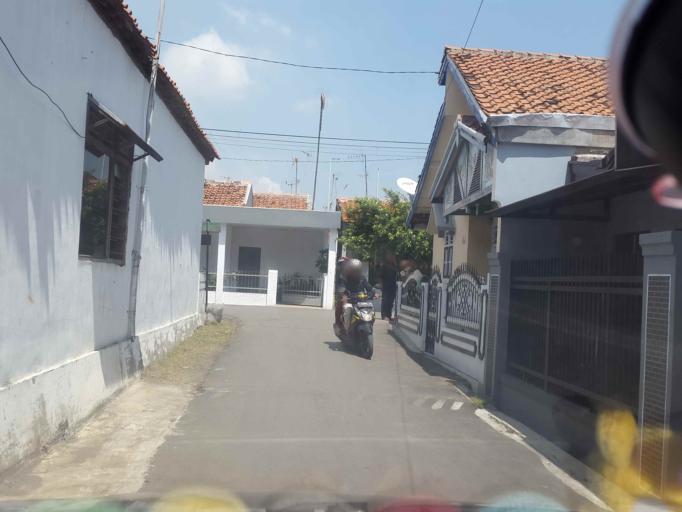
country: ID
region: Central Java
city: Tegal
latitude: -6.8611
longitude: 109.1448
